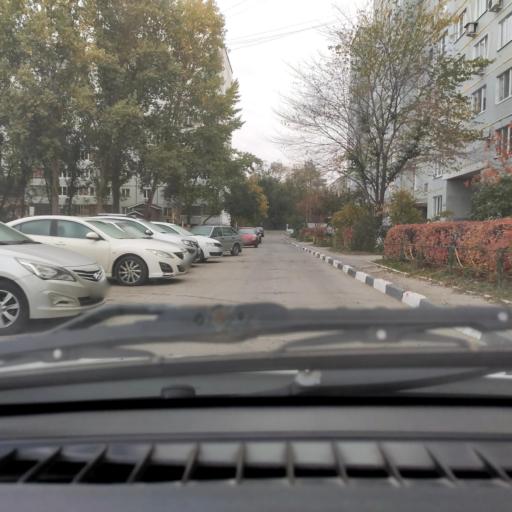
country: RU
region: Samara
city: Zhigulevsk
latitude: 53.4790
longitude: 49.4642
